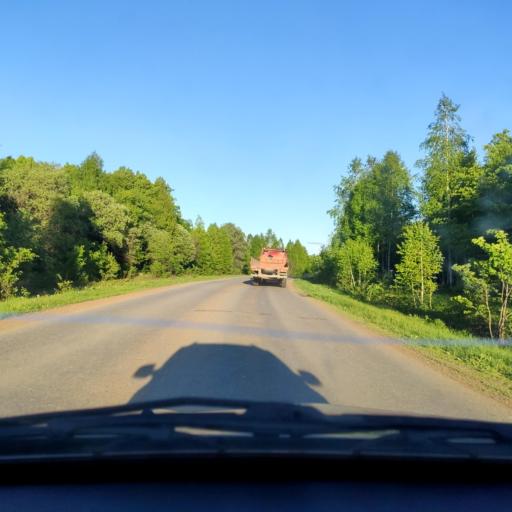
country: RU
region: Bashkortostan
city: Blagoveshchensk
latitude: 55.0331
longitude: 56.0938
